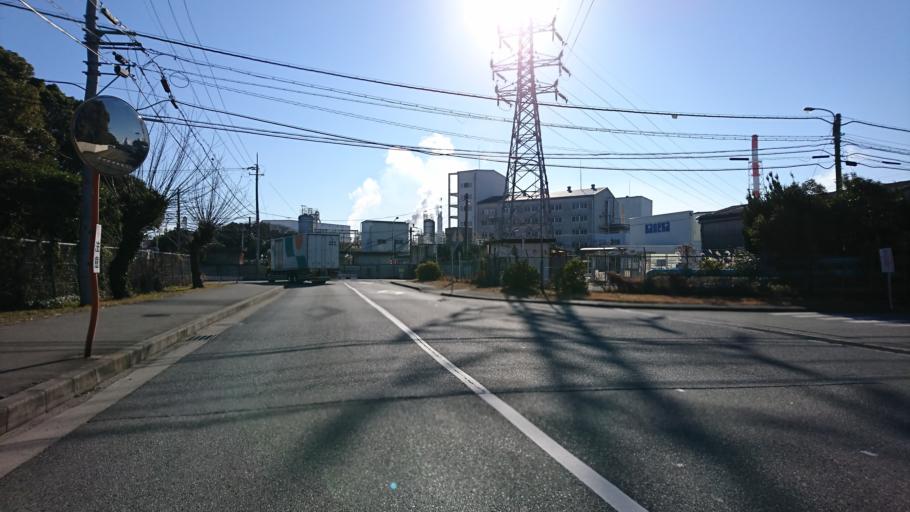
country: JP
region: Hyogo
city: Kakogawacho-honmachi
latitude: 34.7427
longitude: 134.7969
